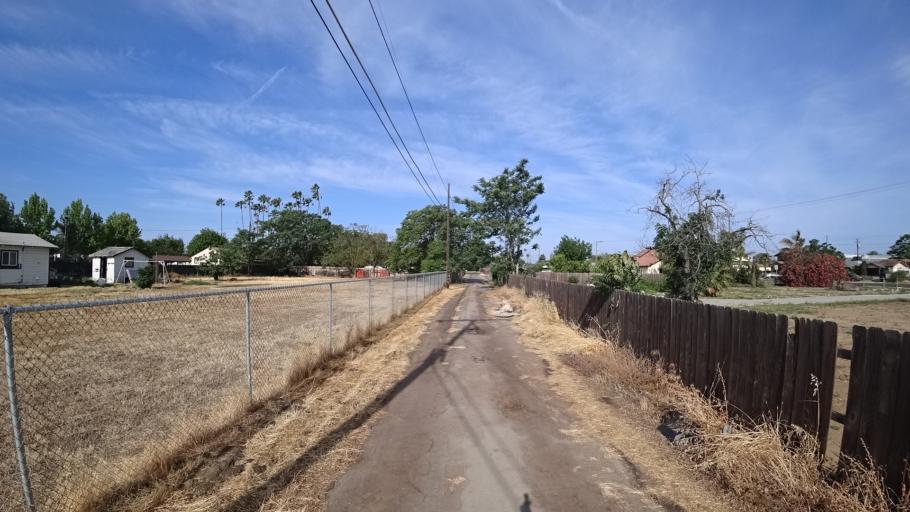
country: US
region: California
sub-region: Kings County
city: Hanford
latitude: 36.3211
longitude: -119.6430
